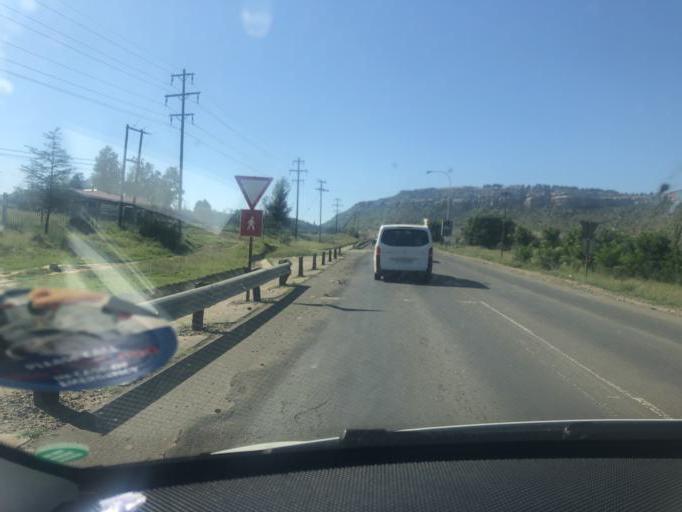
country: LS
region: Maseru
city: Maseru
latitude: -29.3266
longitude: 27.4742
